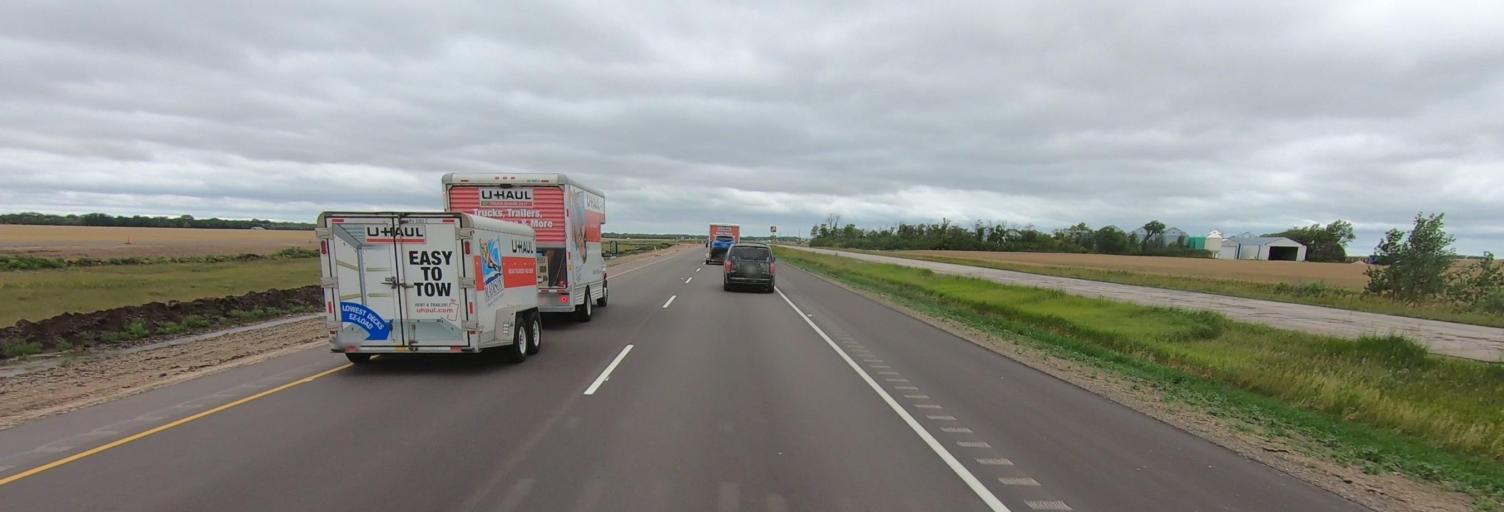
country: CA
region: Manitoba
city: Headingley
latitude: 49.8807
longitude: -97.4519
